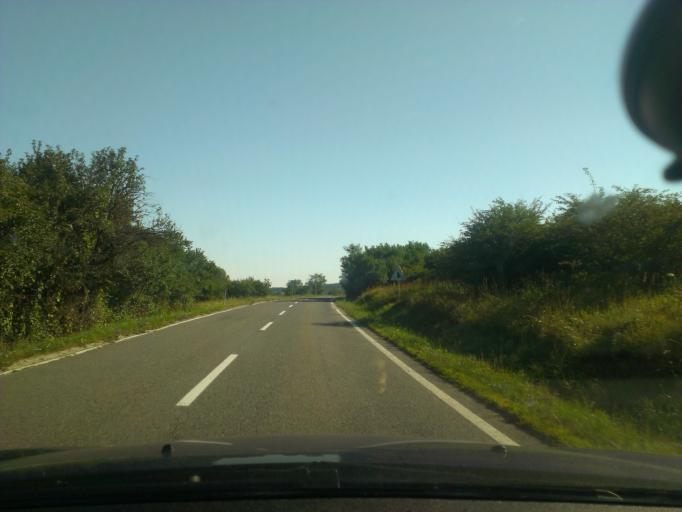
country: CZ
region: South Moravian
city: Velka nad Velickou
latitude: 48.8245
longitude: 17.5143
